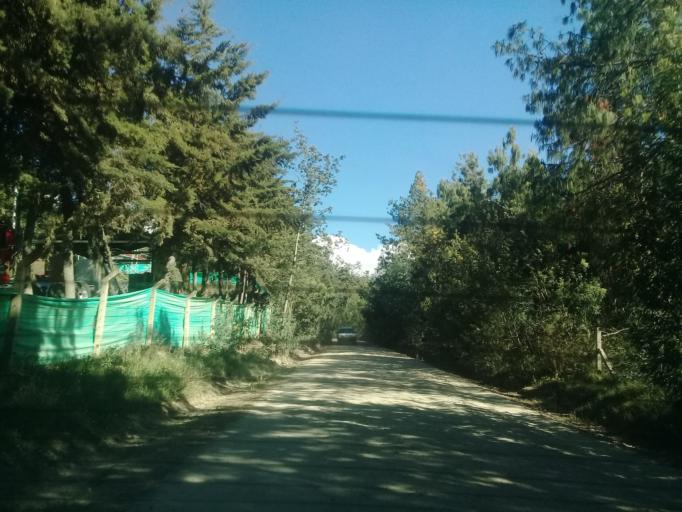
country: CO
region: Cundinamarca
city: Guasca
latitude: 4.9002
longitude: -73.8833
